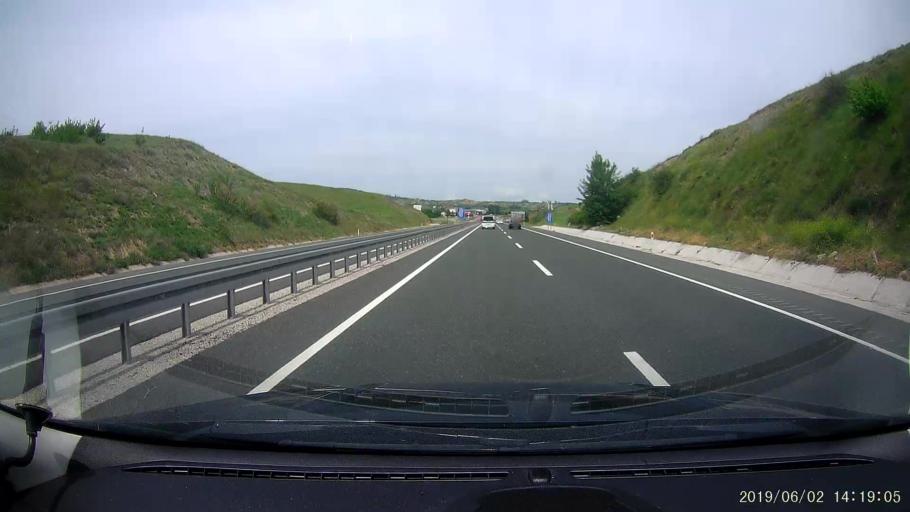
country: TR
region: Kastamonu
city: Tosya
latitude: 40.9605
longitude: 33.9706
